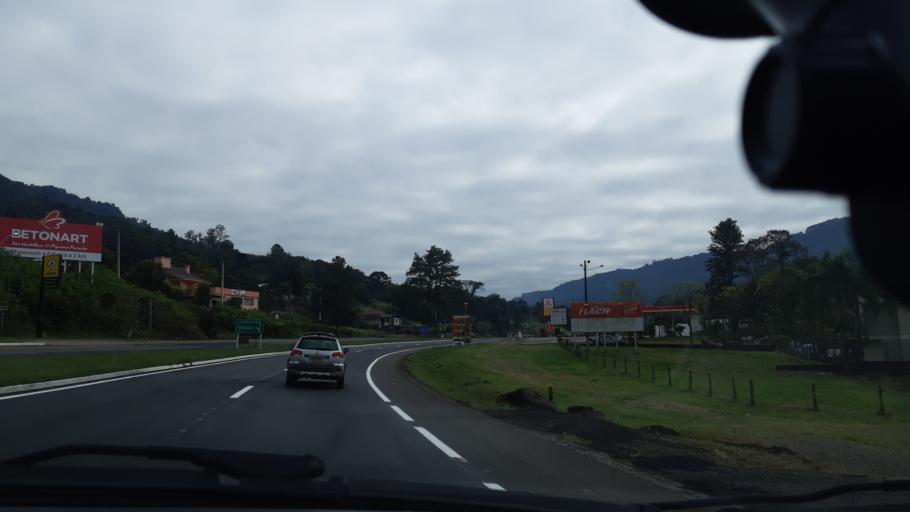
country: BR
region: Rio Grande do Sul
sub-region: Farroupilha
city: Farroupilha
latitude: -29.3993
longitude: -51.3578
